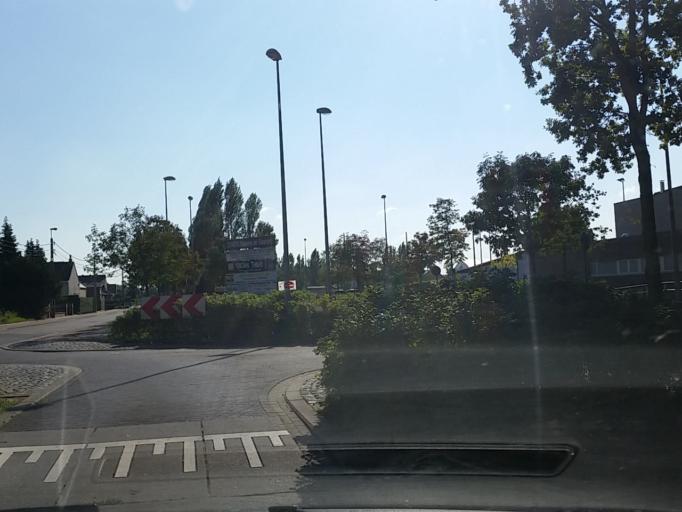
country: BE
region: Flanders
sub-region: Provincie Vlaams-Brabant
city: Zemst
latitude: 50.9714
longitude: 4.5009
